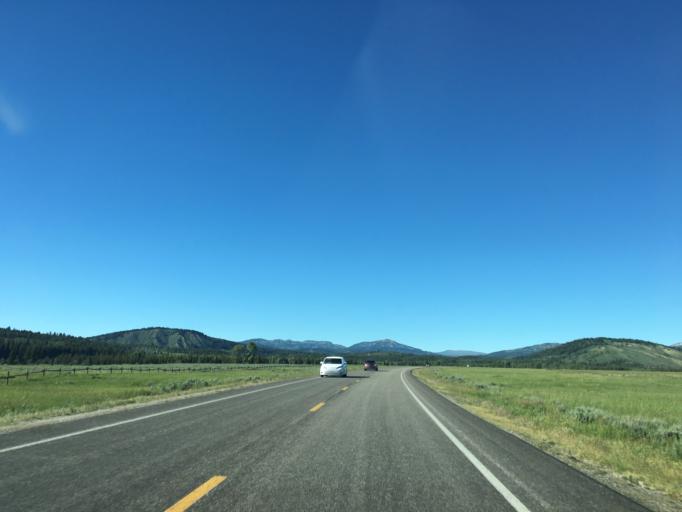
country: US
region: Wyoming
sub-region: Teton County
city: Jackson
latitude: 43.8172
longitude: -110.5251
